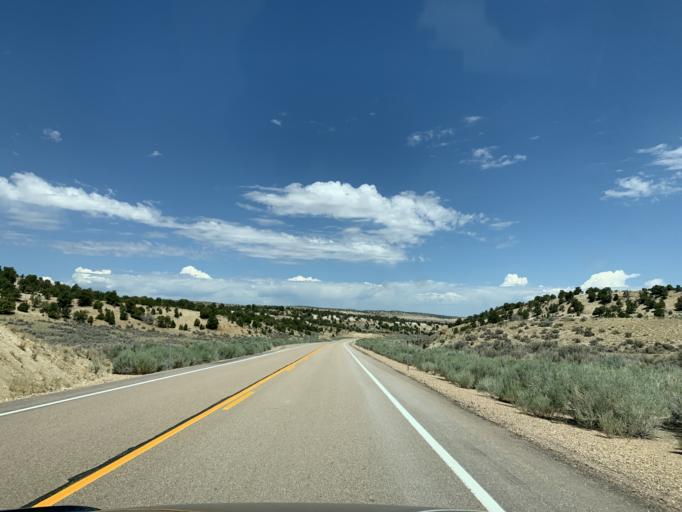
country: US
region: Utah
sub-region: Duchesne County
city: Duchesne
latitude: 39.9081
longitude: -110.2306
